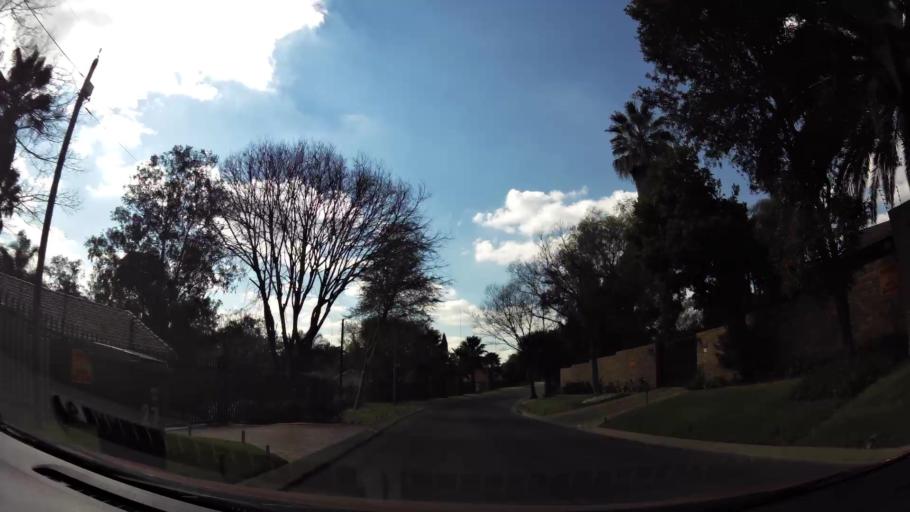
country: ZA
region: Gauteng
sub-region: City of Johannesburg Metropolitan Municipality
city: Roodepoort
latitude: -26.0738
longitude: 27.9501
